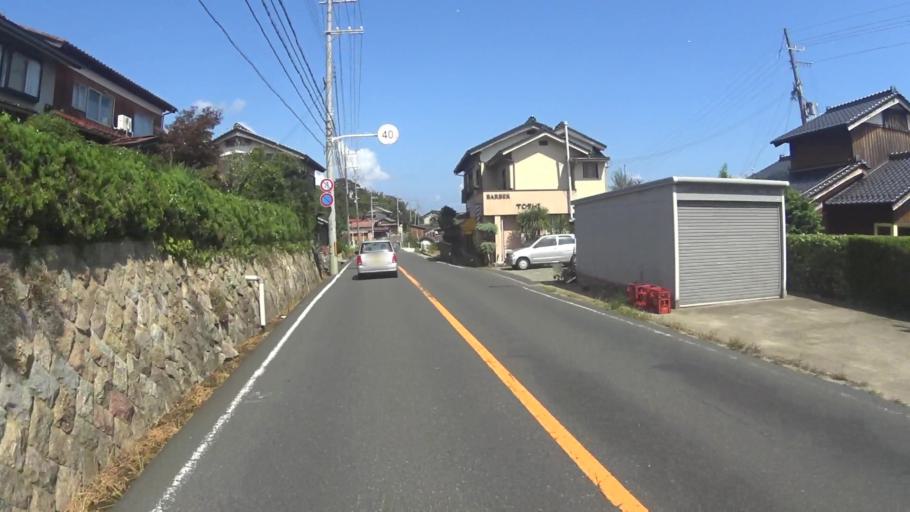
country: JP
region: Kyoto
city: Miyazu
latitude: 35.6001
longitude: 135.2165
